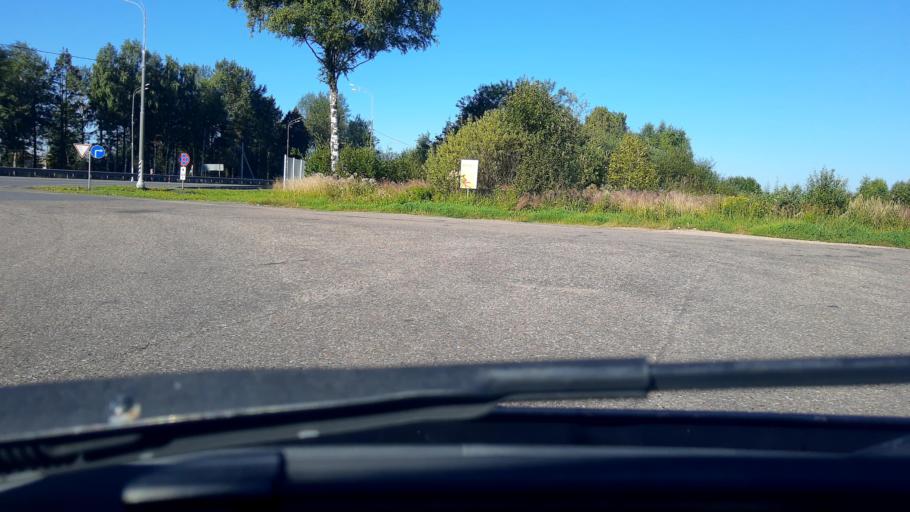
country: RU
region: Smolensk
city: Safonovo
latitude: 55.1287
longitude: 33.1507
